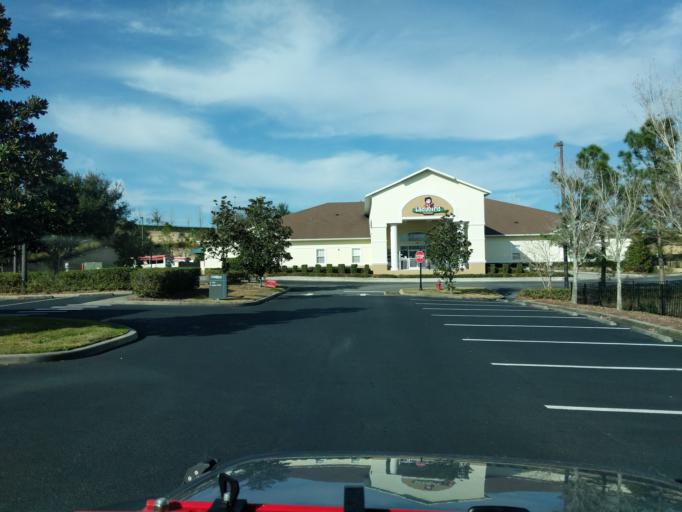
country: US
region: Florida
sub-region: Lake County
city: Minneola
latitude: 28.5474
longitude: -81.7115
